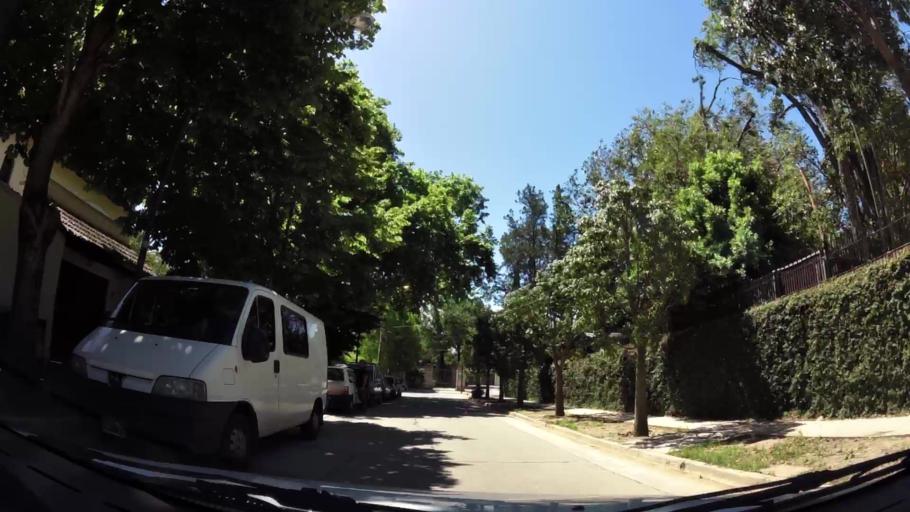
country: AR
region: Buenos Aires
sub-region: Partido de San Isidro
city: San Isidro
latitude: -34.4754
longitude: -58.4927
